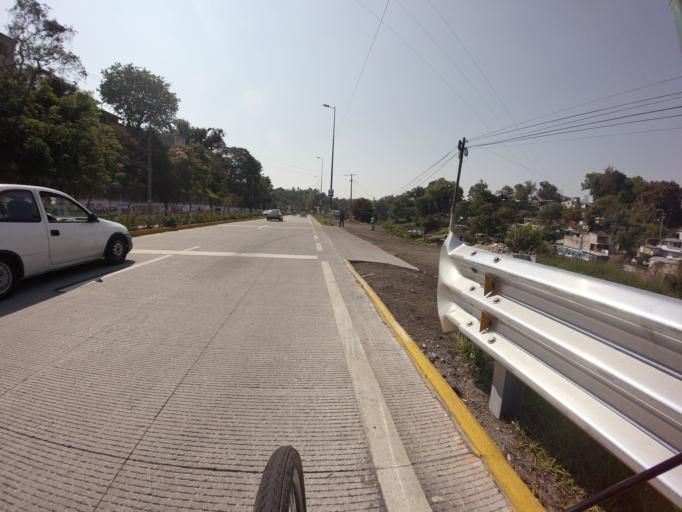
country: MX
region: Veracruz
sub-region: Xalapa
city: Xalapa de Enriquez
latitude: 19.5155
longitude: -96.9324
